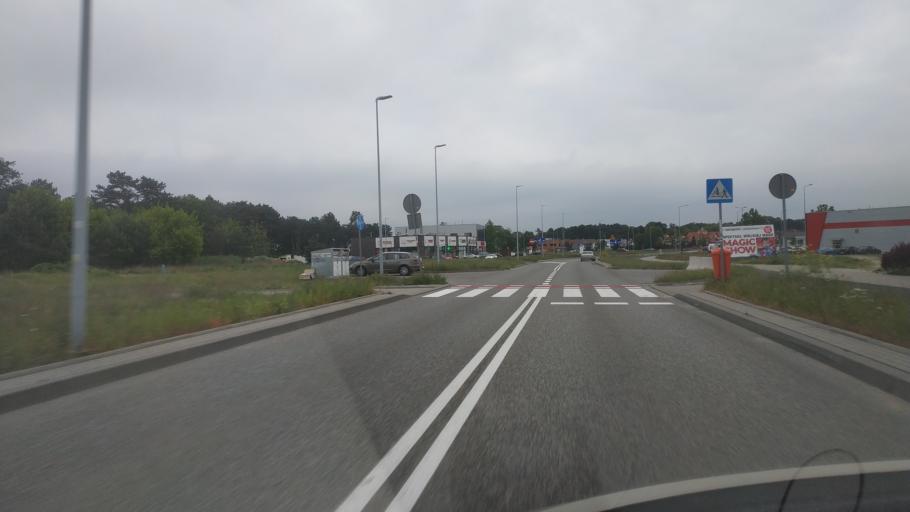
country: PL
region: Kujawsko-Pomorskie
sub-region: Torun
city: Torun
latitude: 53.0427
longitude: 18.6002
